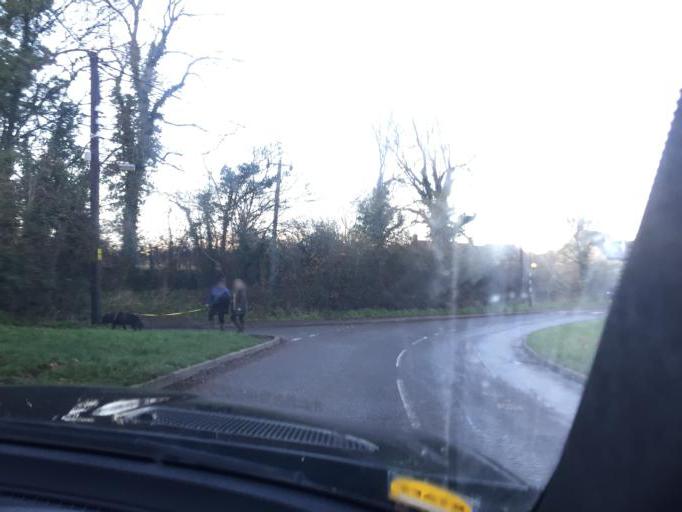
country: GB
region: England
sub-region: Northamptonshire
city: Brackley
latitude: 52.0874
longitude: -1.1464
